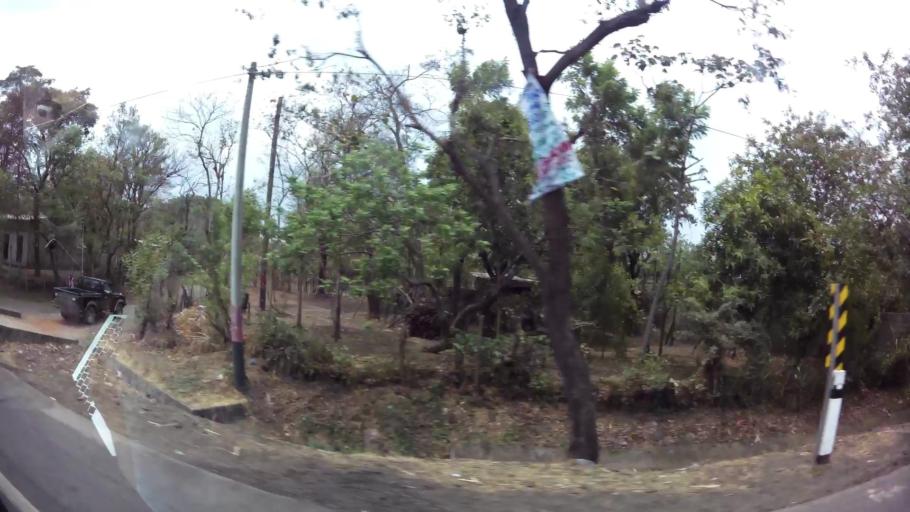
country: NI
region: Leon
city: Telica
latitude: 12.5254
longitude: -86.8774
